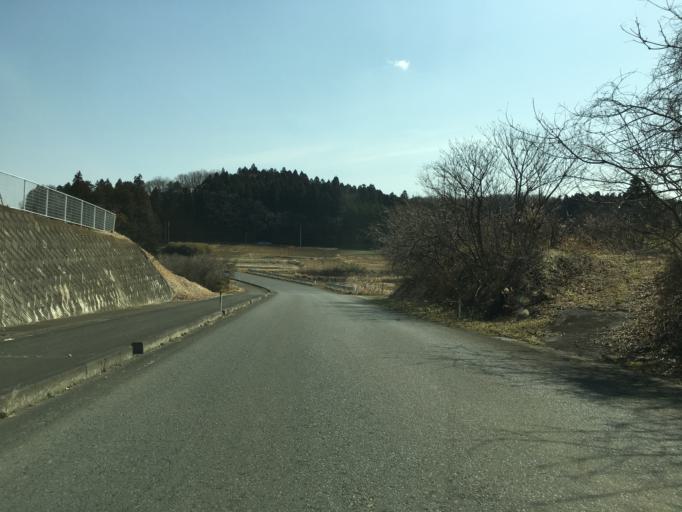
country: JP
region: Fukushima
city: Ishikawa
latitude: 37.1393
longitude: 140.3986
